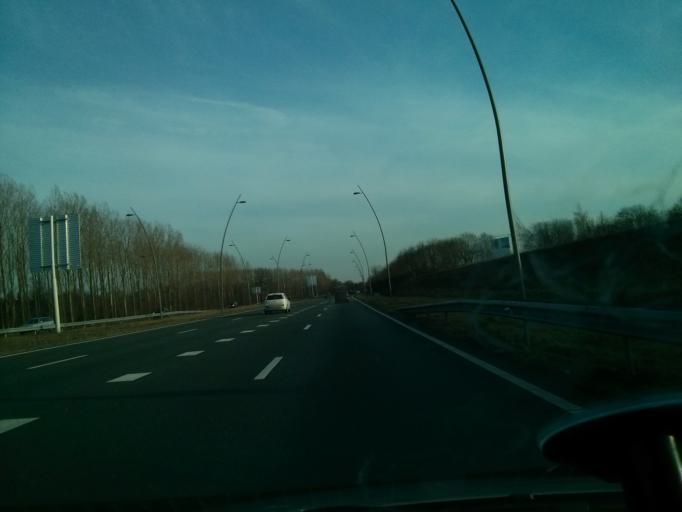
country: NL
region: North Brabant
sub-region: Gemeente Son en Breugel
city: Son
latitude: 51.4961
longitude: 5.4794
